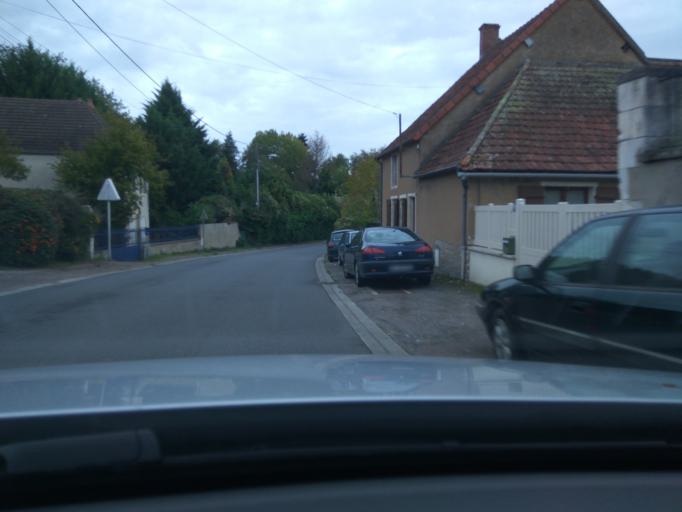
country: FR
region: Bourgogne
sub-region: Departement de la Nievre
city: Cosne-Cours-sur-Loire
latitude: 47.3684
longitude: 2.8991
